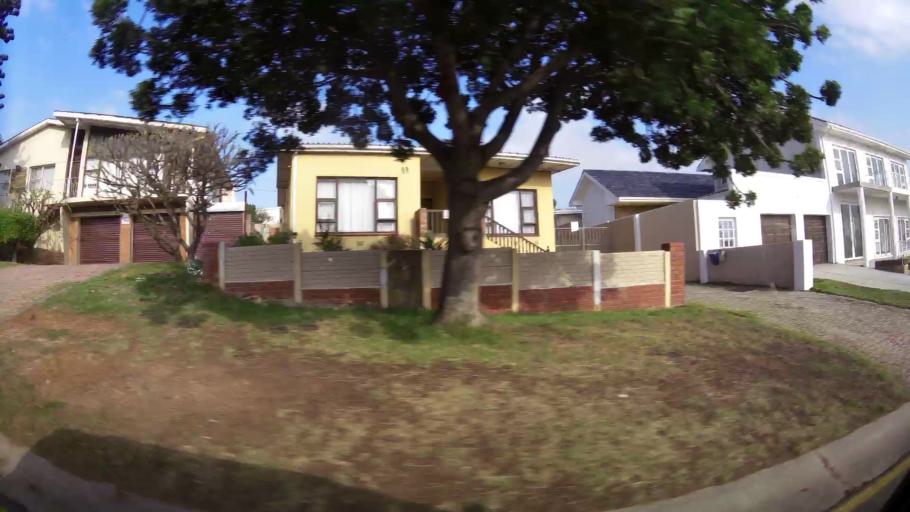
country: ZA
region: Eastern Cape
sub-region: Nelson Mandela Bay Metropolitan Municipality
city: Port Elizabeth
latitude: -33.9265
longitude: 25.5549
